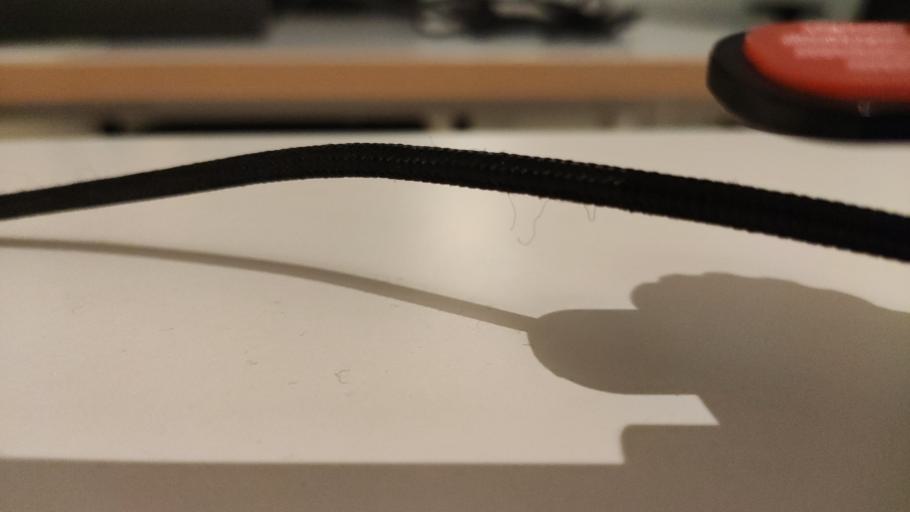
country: RU
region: Moskovskaya
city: Meshcherino
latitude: 55.2011
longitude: 38.3742
